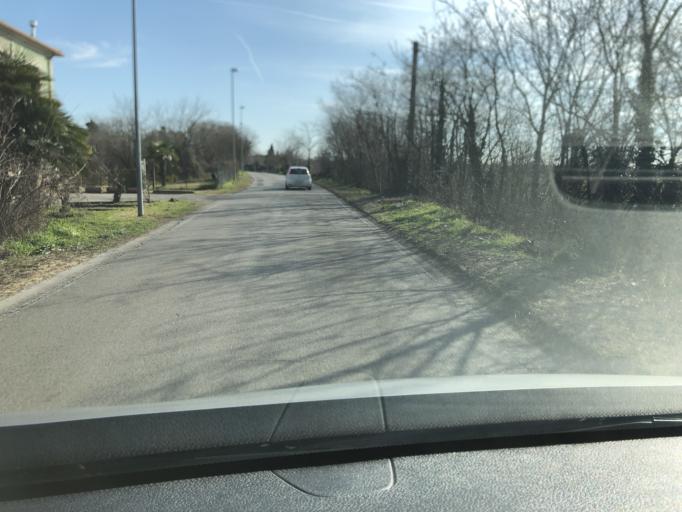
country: IT
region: Veneto
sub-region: Provincia di Verona
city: Verona
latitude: 45.4321
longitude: 10.9475
